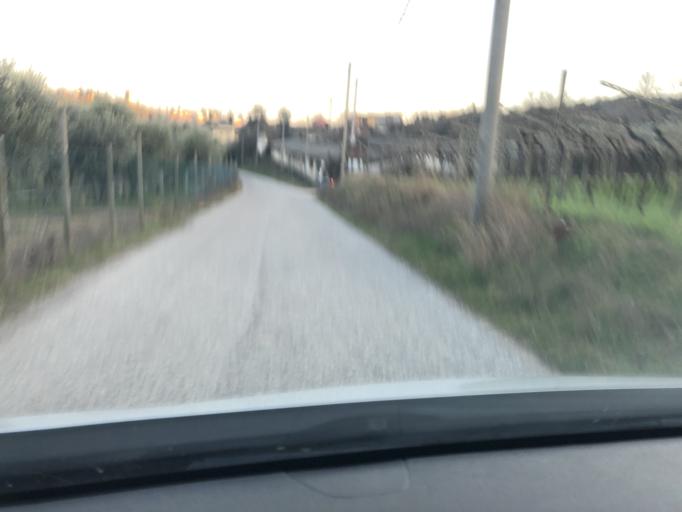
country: IT
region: Veneto
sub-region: Provincia di Verona
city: Sandra
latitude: 45.4592
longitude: 10.8128
